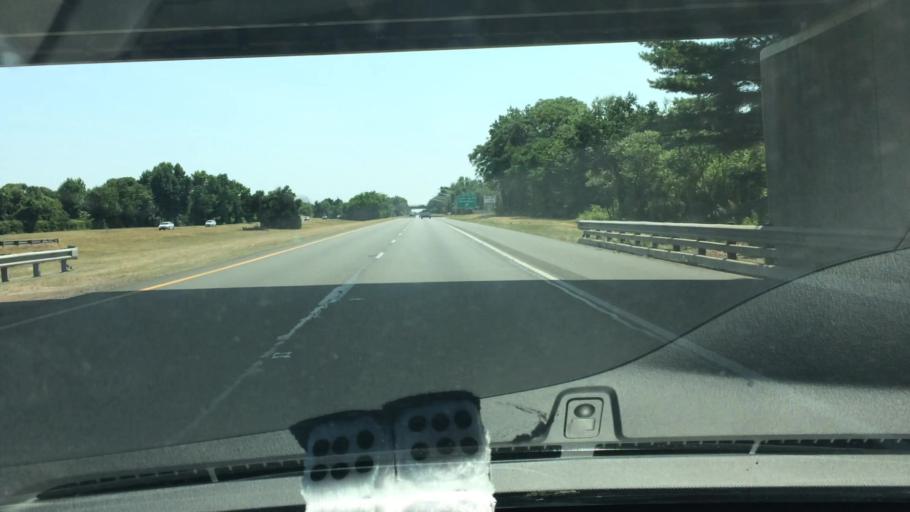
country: US
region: New Jersey
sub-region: Gloucester County
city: Beckett
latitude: 39.7656
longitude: -75.3563
